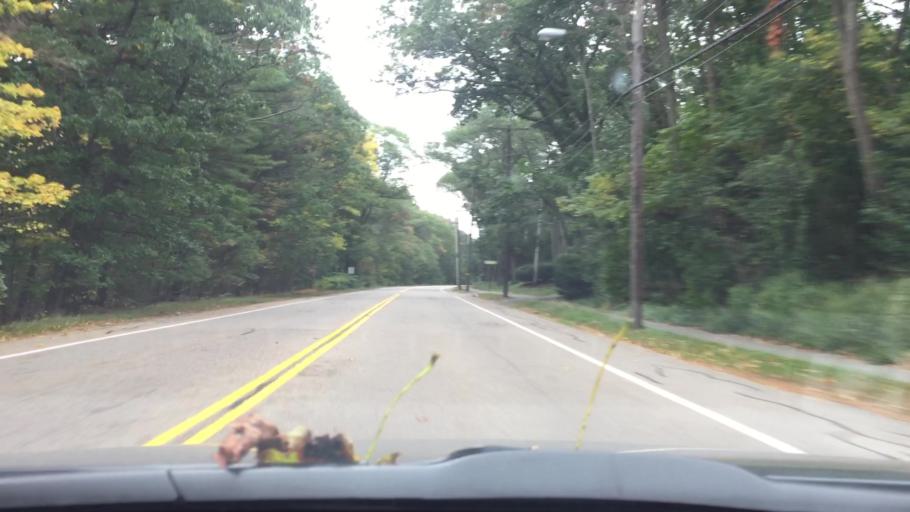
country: US
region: Massachusetts
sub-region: Norfolk County
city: Needham
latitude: 42.2883
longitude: -71.2121
